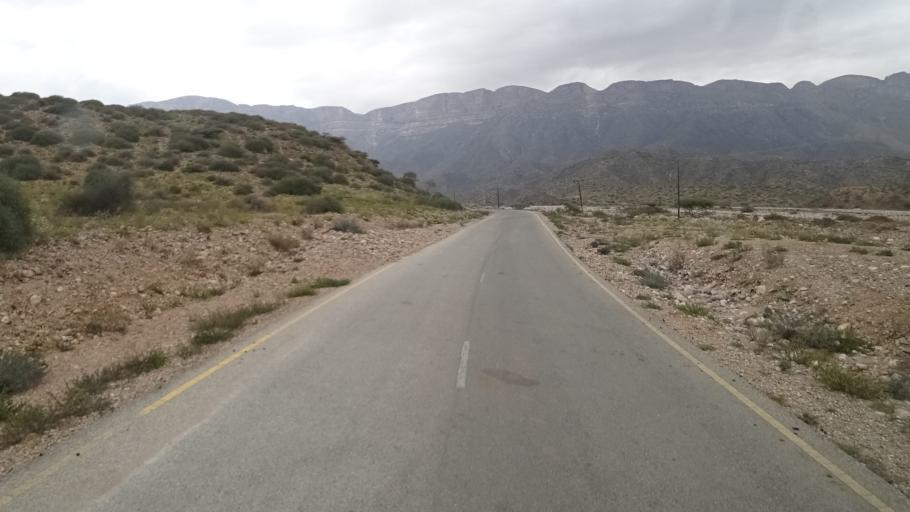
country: OM
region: Zufar
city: Salalah
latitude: 17.1695
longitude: 54.9741
